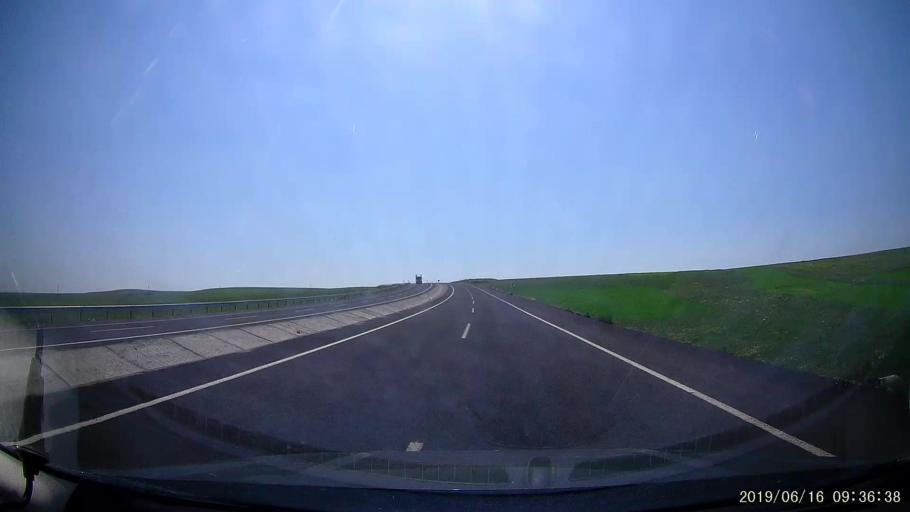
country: TR
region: Kars
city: Kars
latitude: 40.5565
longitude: 43.1765
